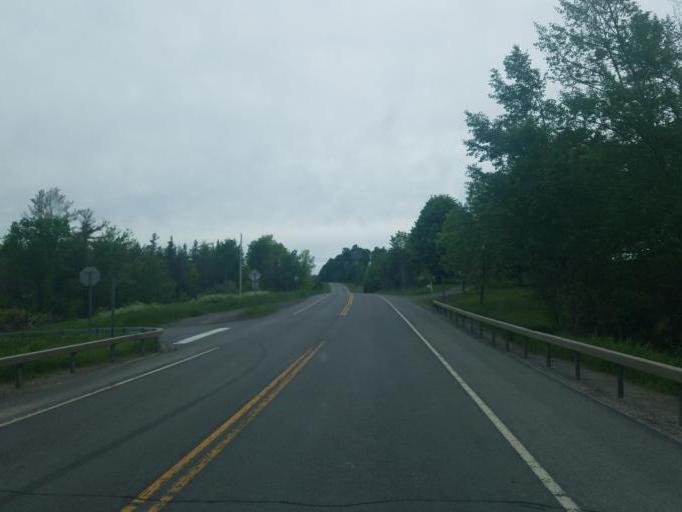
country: US
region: New York
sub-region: Herkimer County
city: Ilion
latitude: 42.9110
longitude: -75.1213
